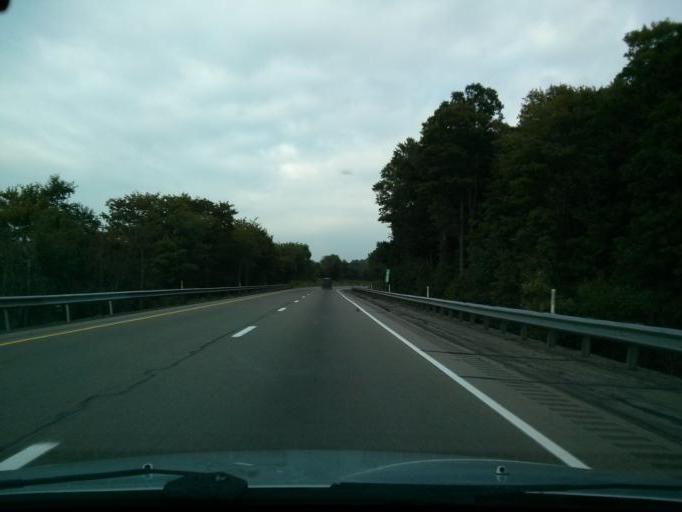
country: US
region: Pennsylvania
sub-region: Jefferson County
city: Brookville
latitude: 41.1697
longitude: -79.0203
